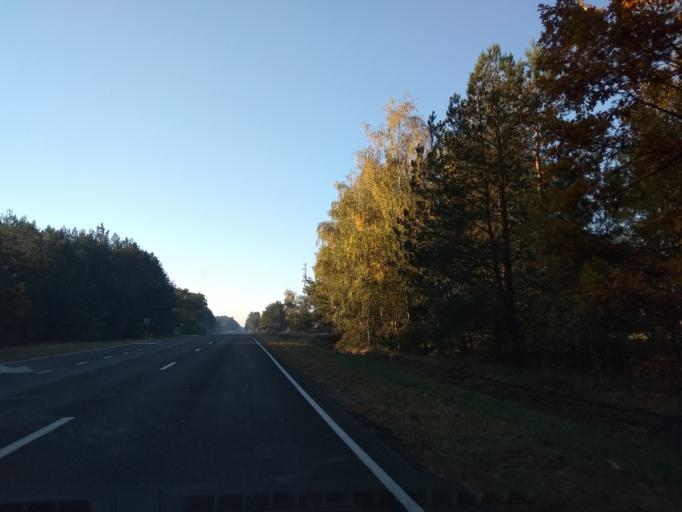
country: BY
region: Brest
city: Kobryn
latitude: 52.0568
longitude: 24.2805
